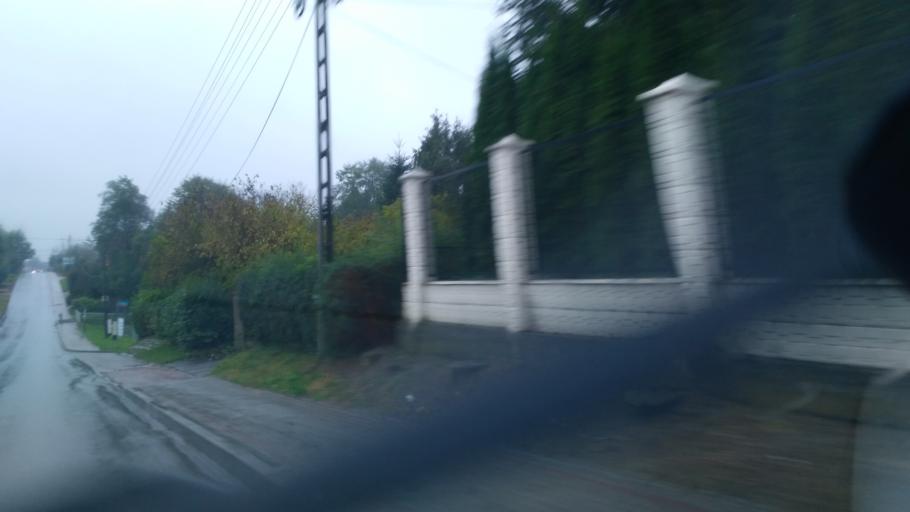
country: PL
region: Subcarpathian Voivodeship
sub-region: Powiat krosnienski
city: Miejsce Piastowe
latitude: 49.6512
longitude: 21.8085
